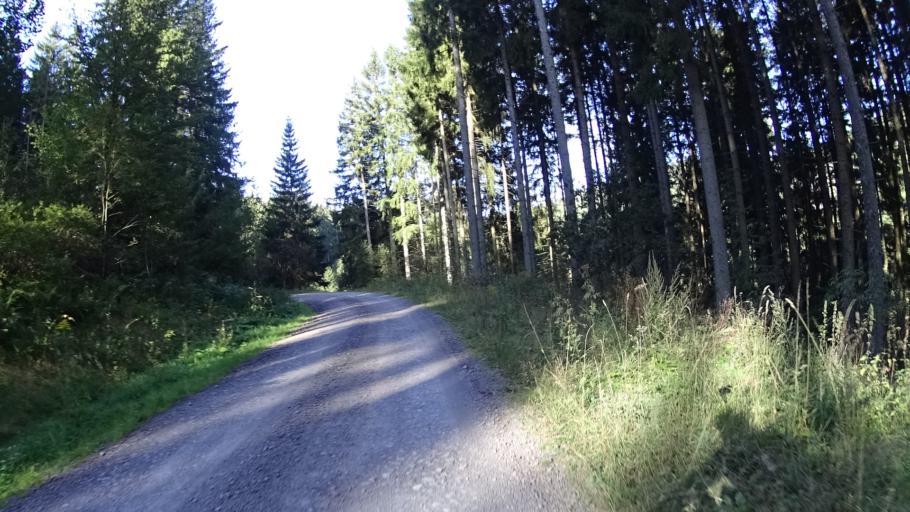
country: DE
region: Thuringia
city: Langewiesen
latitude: 50.6441
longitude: 10.9477
